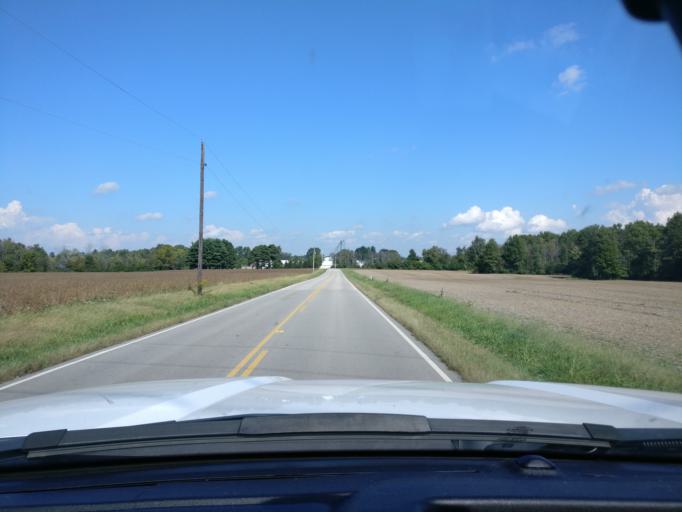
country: US
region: Ohio
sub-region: Warren County
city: Waynesville
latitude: 39.4731
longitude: -83.9943
